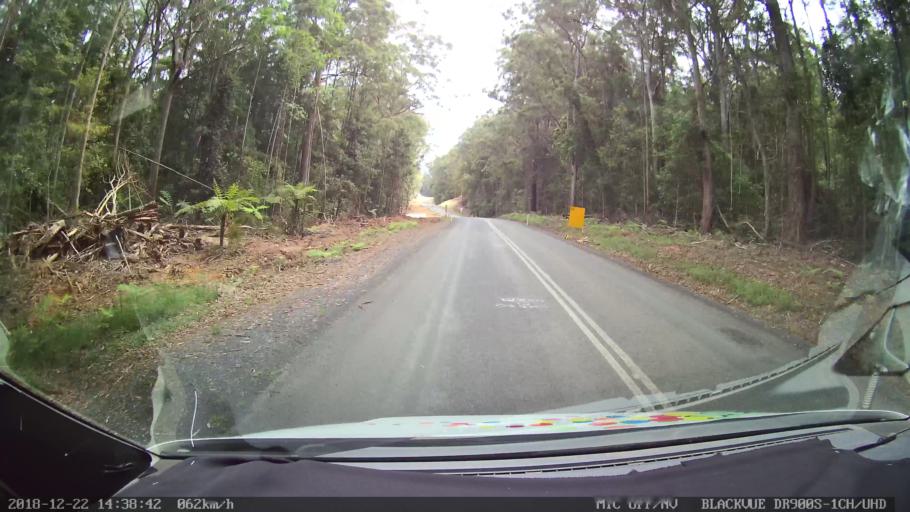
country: AU
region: New South Wales
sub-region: Bellingen
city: Dorrigo
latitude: -30.1403
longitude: 152.5958
